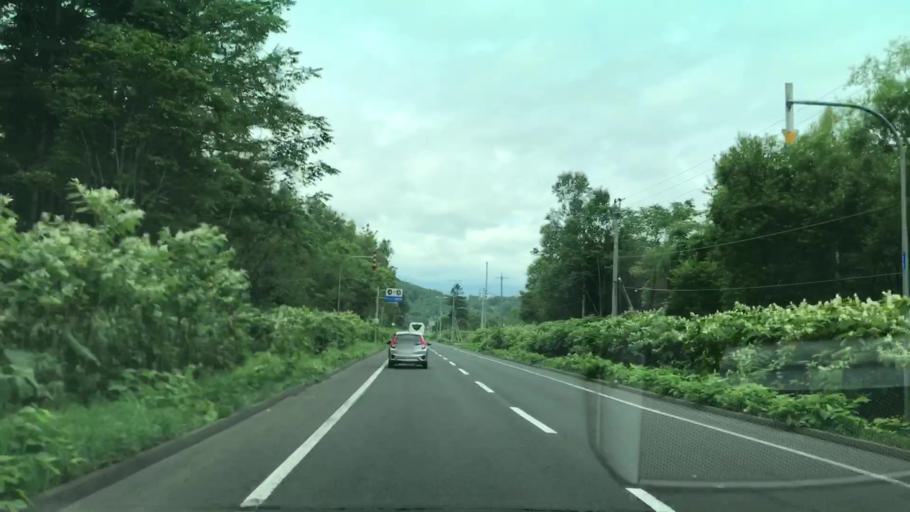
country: JP
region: Hokkaido
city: Niseko Town
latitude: 42.9479
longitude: 140.8493
